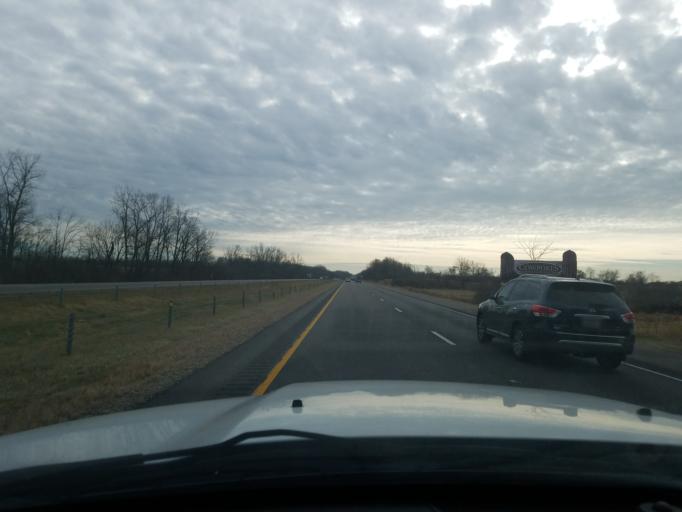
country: US
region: Indiana
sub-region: Delaware County
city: Yorktown
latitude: 40.2487
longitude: -85.5575
